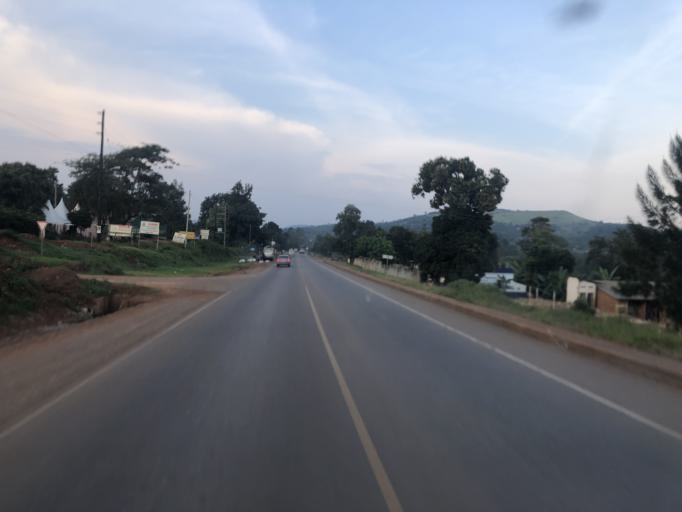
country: UG
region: Central Region
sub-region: Mpigi District
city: Mpigi
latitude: 0.2215
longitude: 32.3356
